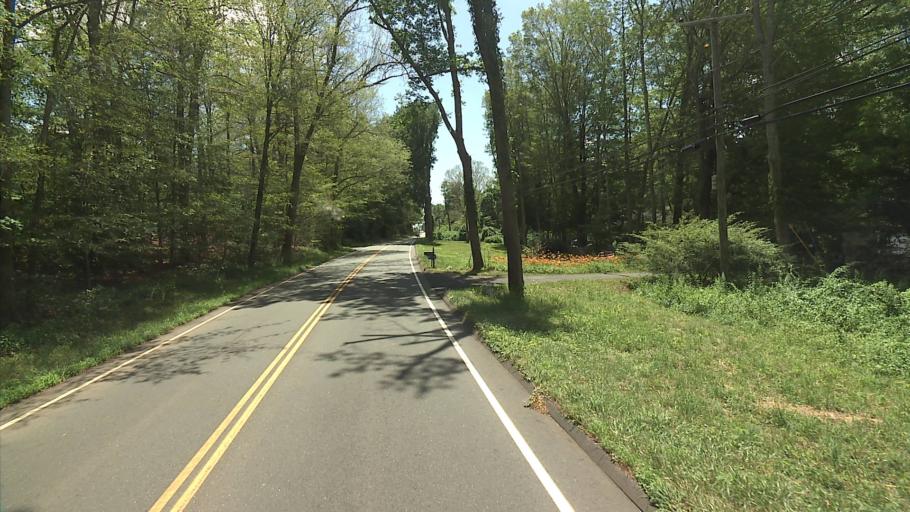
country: US
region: Connecticut
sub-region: Middlesex County
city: Moodus
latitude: 41.4885
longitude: -72.4472
